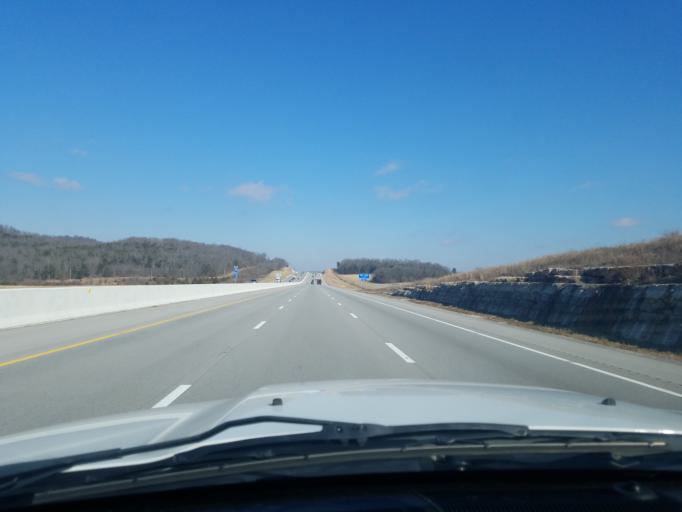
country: US
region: Kentucky
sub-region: Hart County
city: Horse Cave
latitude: 37.2185
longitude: -85.9343
